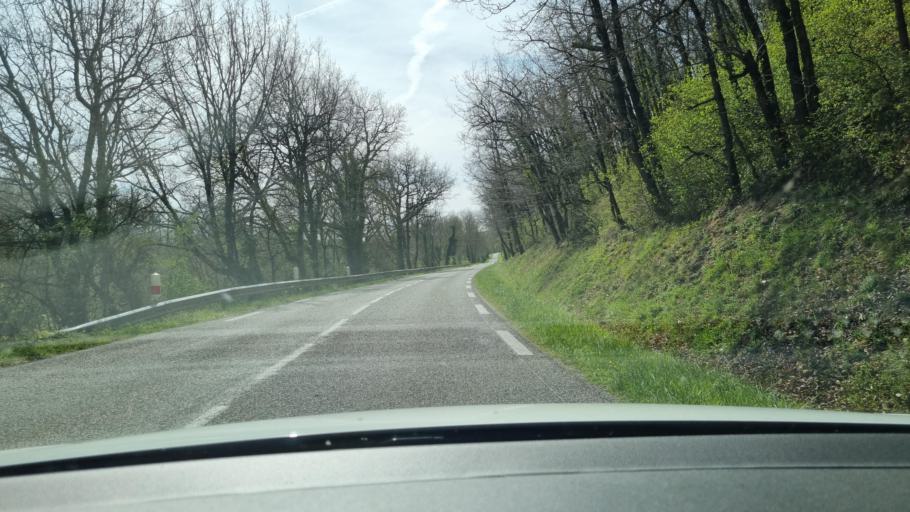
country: FR
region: Midi-Pyrenees
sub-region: Departement du Gers
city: Samatan
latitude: 43.4916
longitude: 0.9956
